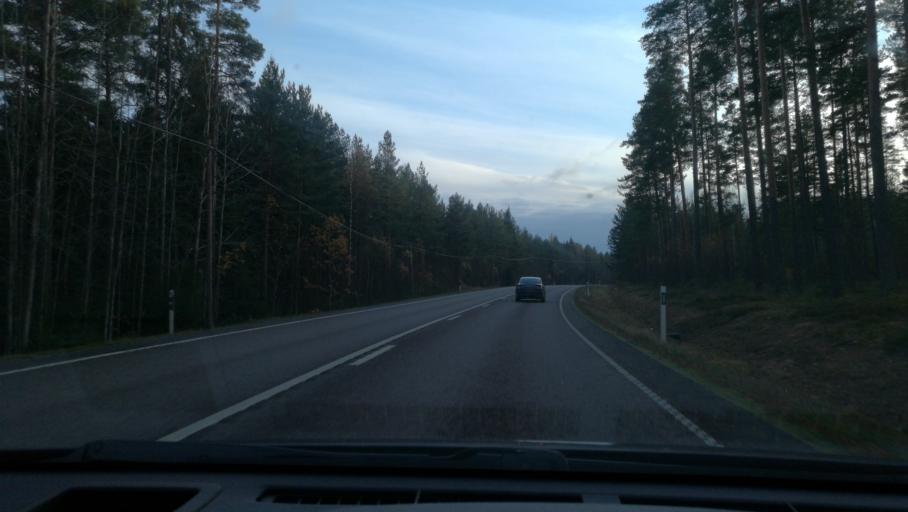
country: SE
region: Soedermanland
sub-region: Katrineholms Kommun
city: Katrineholm
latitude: 59.1744
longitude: 16.1162
